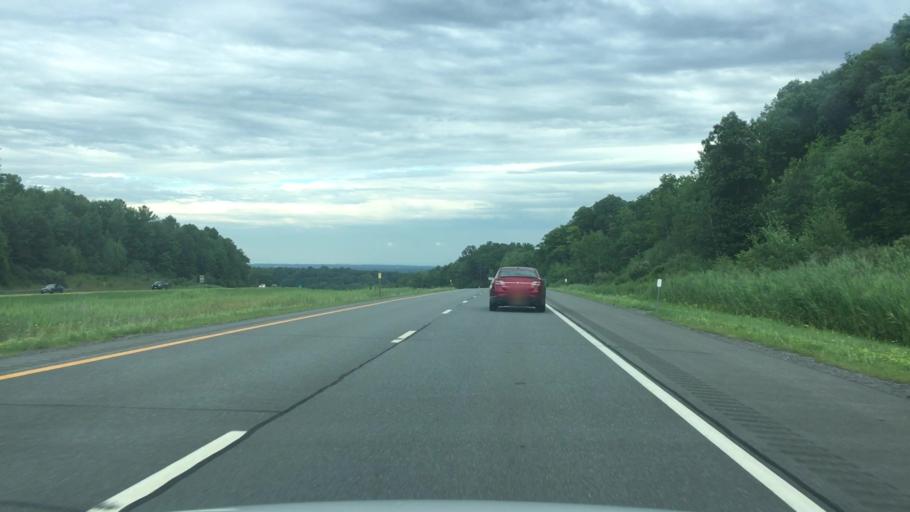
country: US
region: New York
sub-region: Albany County
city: Altamont
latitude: 42.7715
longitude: -74.0691
